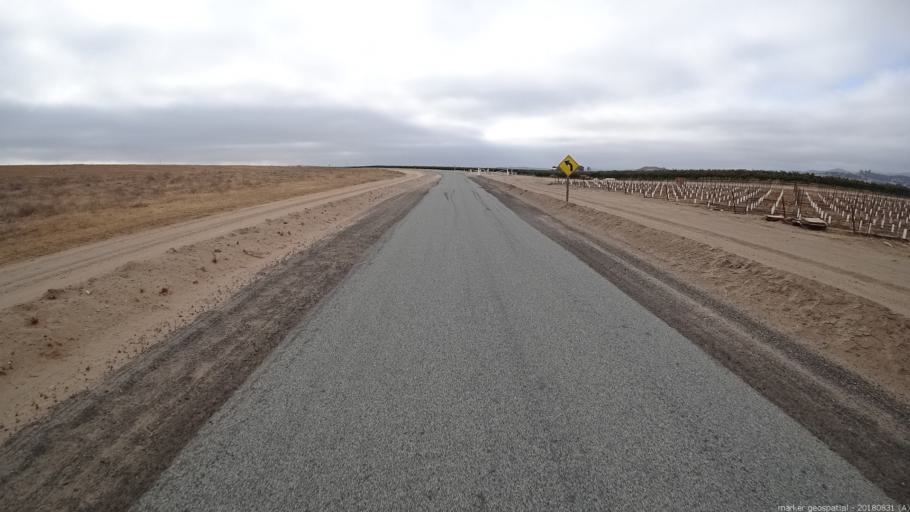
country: US
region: California
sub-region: Monterey County
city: King City
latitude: 36.1550
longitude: -121.1052
